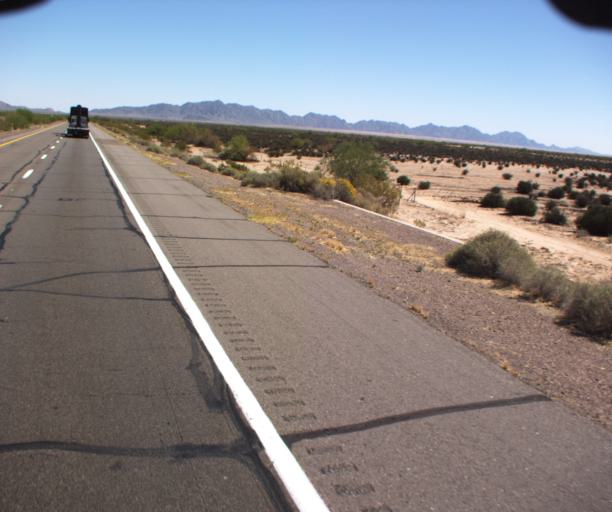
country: US
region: Arizona
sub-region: Yuma County
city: Wellton
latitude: 32.7030
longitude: -113.8900
